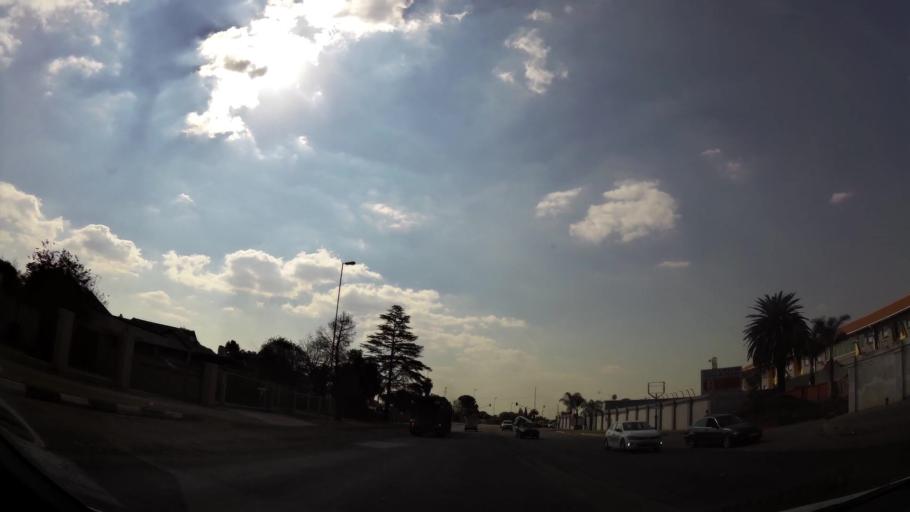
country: ZA
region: Gauteng
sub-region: Ekurhuleni Metropolitan Municipality
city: Boksburg
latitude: -26.1851
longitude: 28.2181
